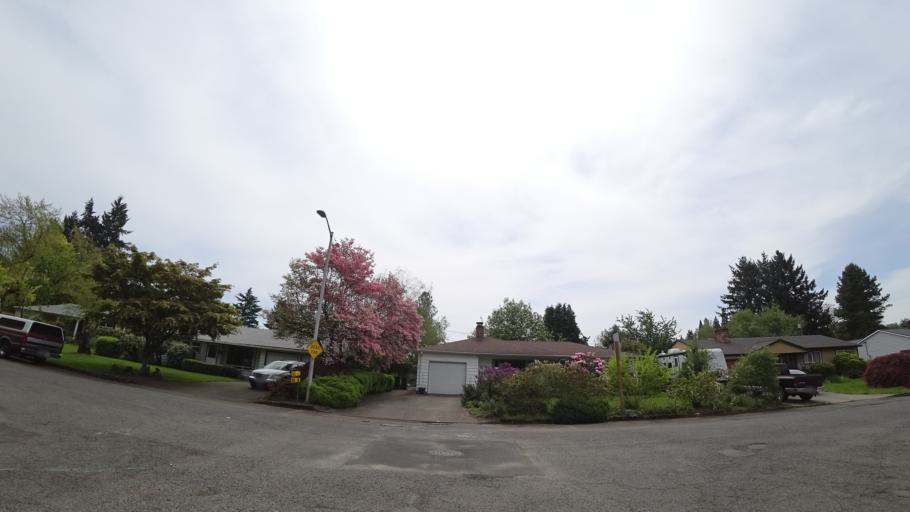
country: US
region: Oregon
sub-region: Clackamas County
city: Milwaukie
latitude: 45.4570
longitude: -122.6228
